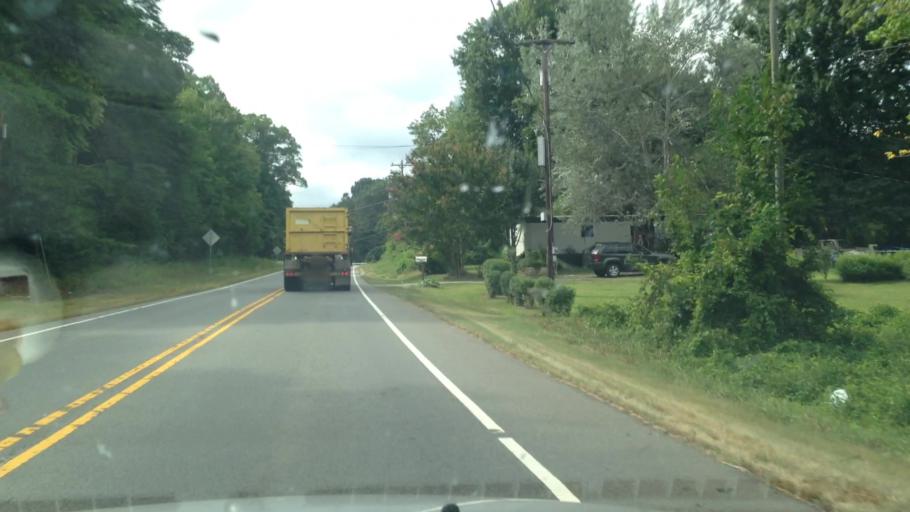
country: US
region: North Carolina
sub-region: Rockingham County
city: Wentworth
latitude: 36.3972
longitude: -79.7584
